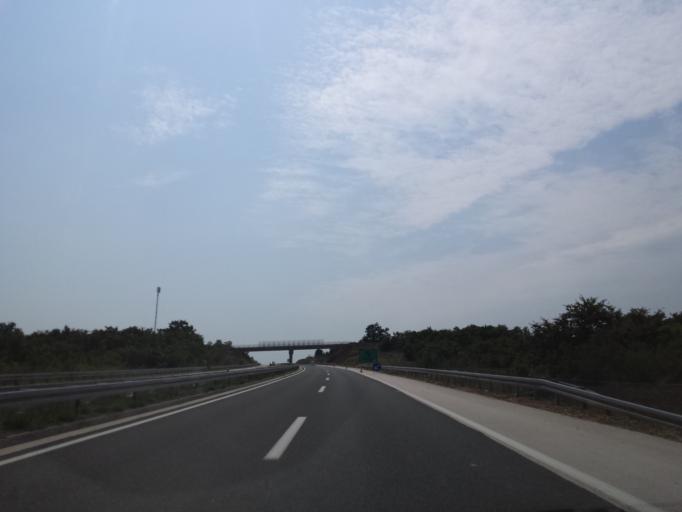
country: HR
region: Zadarska
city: Posedarje
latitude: 44.2091
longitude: 15.4457
